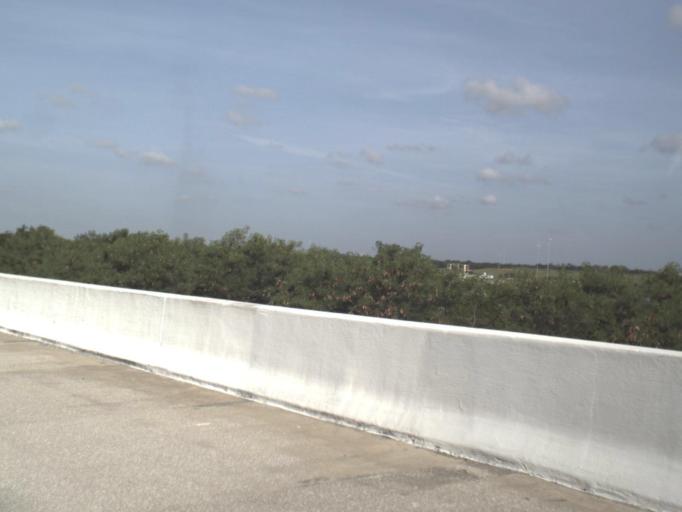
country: US
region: Florida
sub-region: Hillsborough County
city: Palm River-Clair Mel
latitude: 27.9506
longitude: -82.3741
